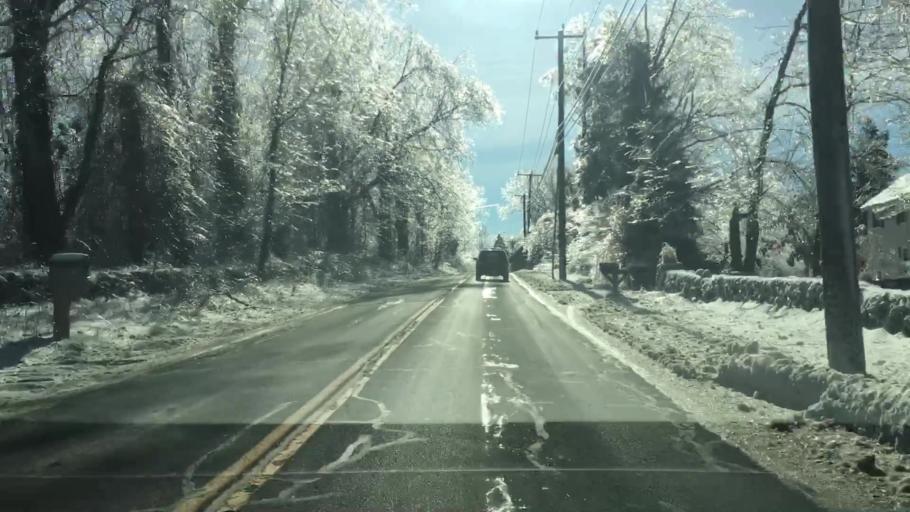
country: US
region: Connecticut
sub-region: Fairfield County
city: Newtown
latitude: 41.3832
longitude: -73.2588
